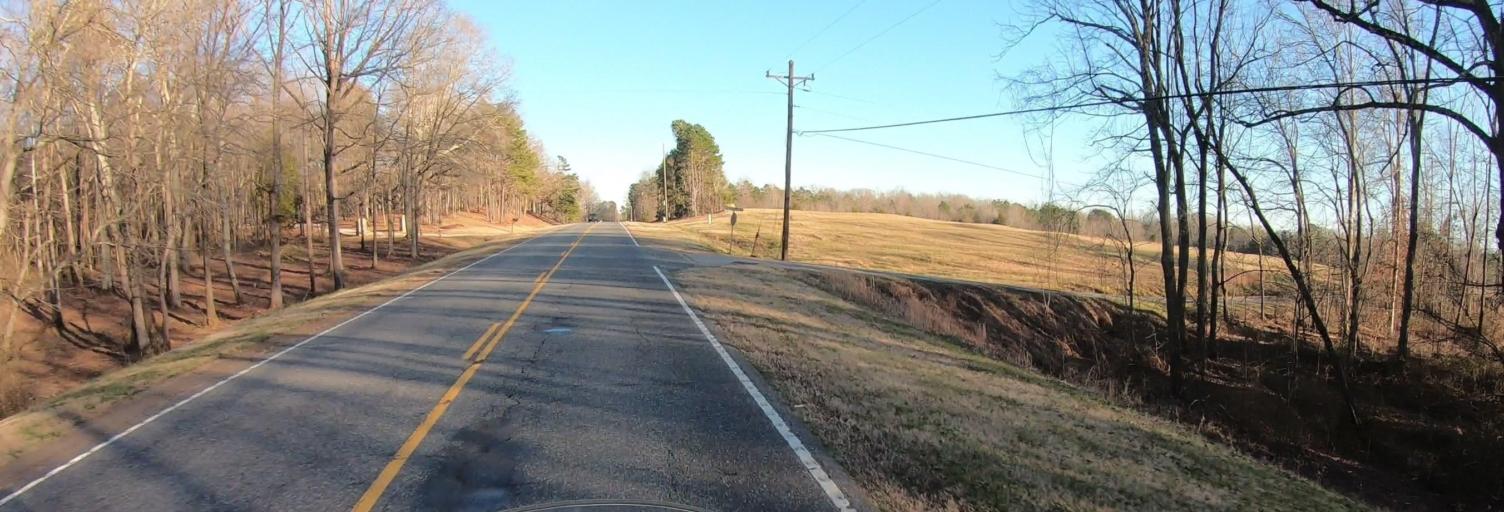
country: US
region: South Carolina
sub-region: Spartanburg County
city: Mayo
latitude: 35.1450
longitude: -81.8403
